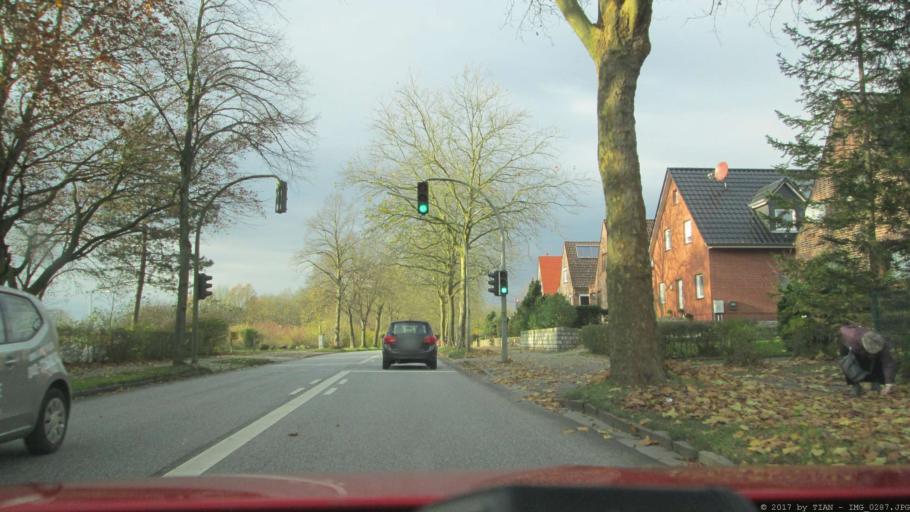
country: DE
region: Hamburg
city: Bergedorf
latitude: 53.4814
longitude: 10.2264
